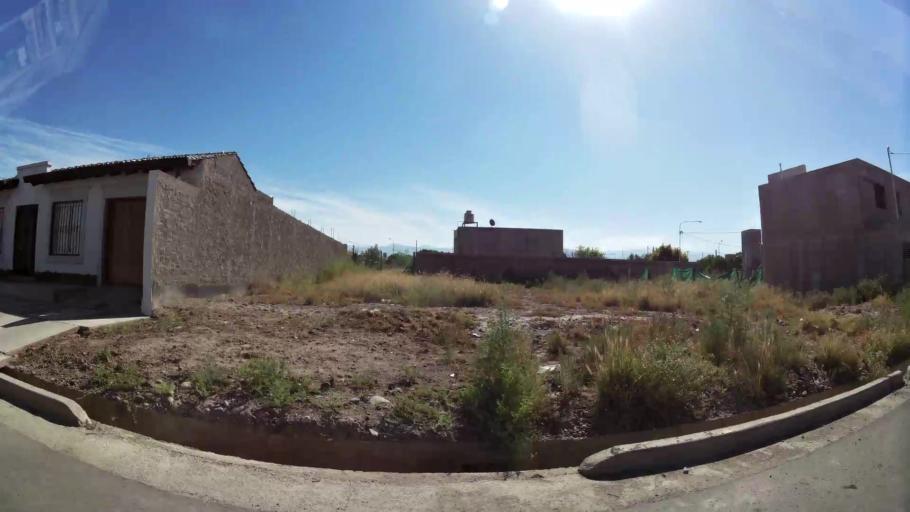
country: AR
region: Mendoza
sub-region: Departamento de Godoy Cruz
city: Godoy Cruz
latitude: -32.9520
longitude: -68.8172
